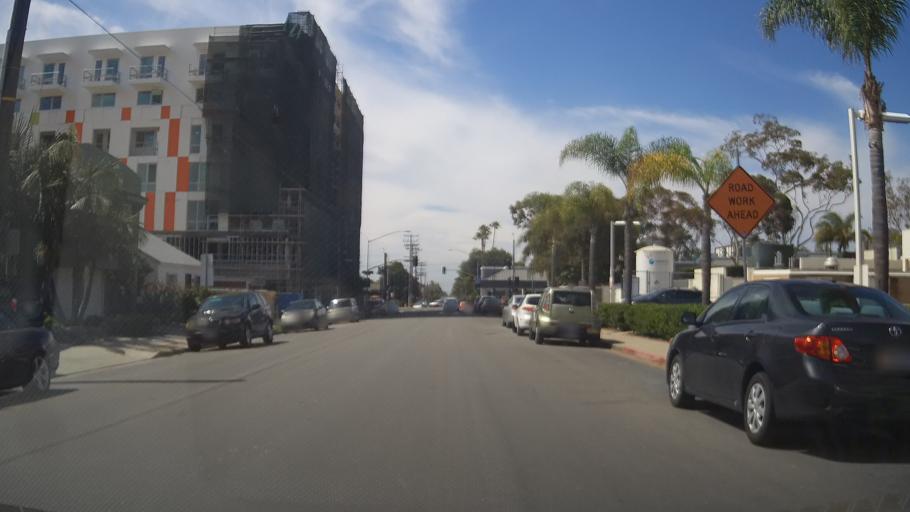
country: US
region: California
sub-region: San Diego County
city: San Diego
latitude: 32.7564
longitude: -117.1438
